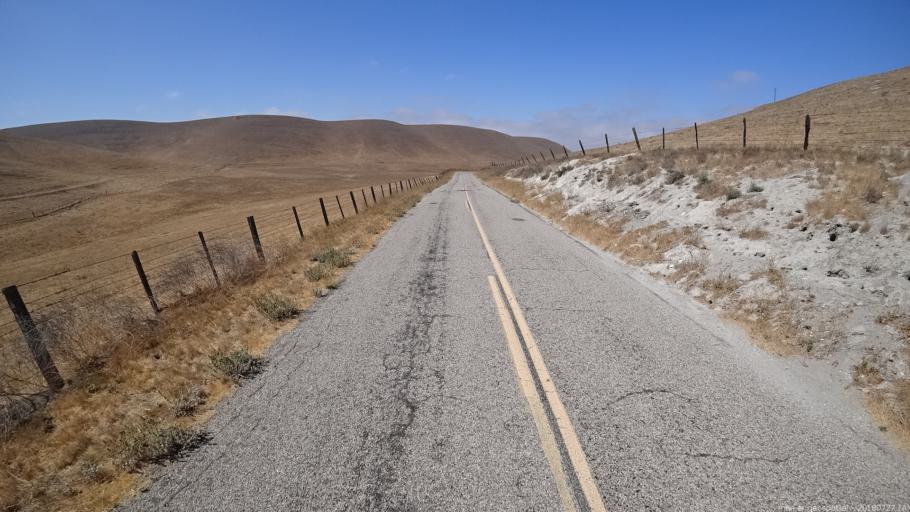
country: US
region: California
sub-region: Monterey County
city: King City
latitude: 36.2484
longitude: -121.0165
